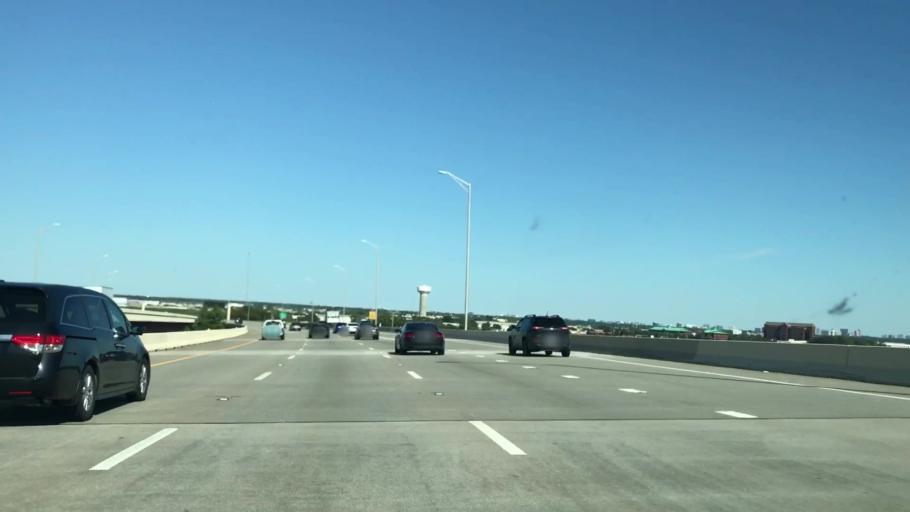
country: US
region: Texas
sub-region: Dallas County
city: Farmers Branch
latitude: 32.9144
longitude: -96.9373
